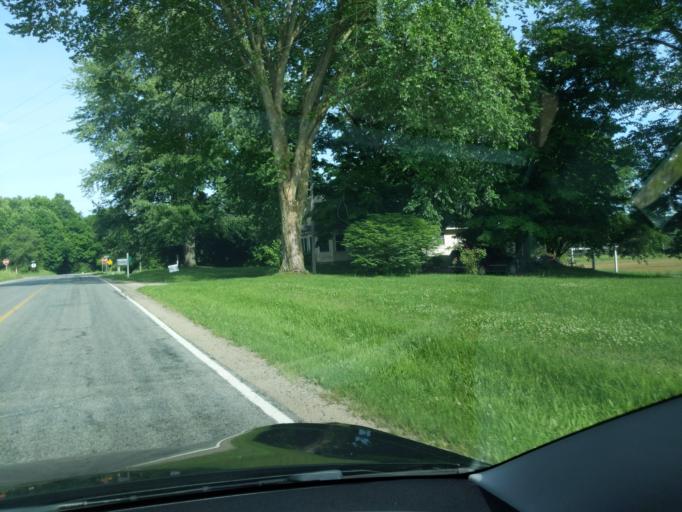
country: US
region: Michigan
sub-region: Newaygo County
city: Fremont
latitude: 43.4238
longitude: -85.9413
